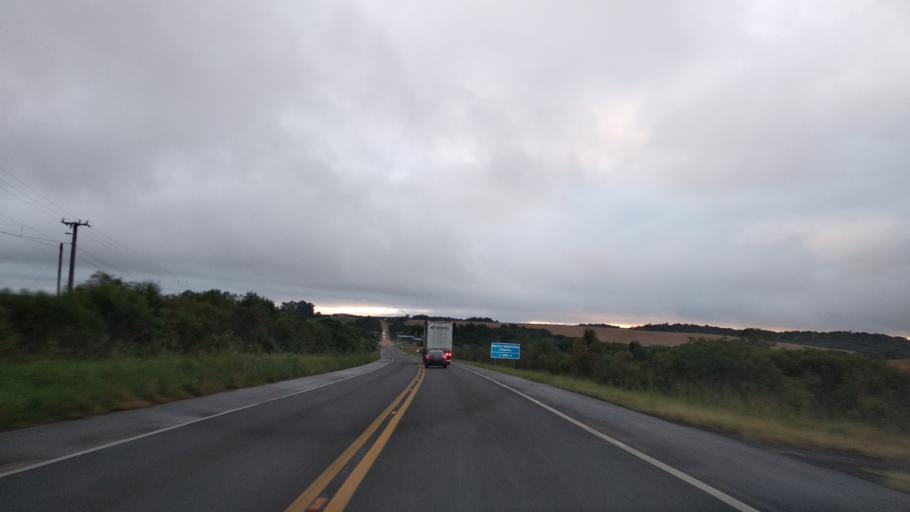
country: BR
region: Santa Catarina
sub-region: Campos Novos
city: Campos Novos
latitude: -27.3896
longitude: -51.1209
